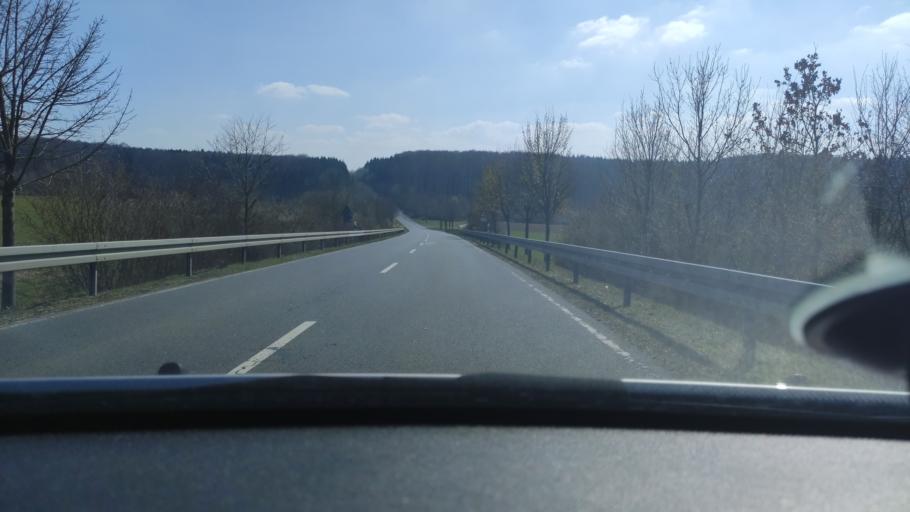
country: DE
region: Baden-Wuerttemberg
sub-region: Regierungsbezirk Stuttgart
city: Assamstadt
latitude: 49.4439
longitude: 9.7017
